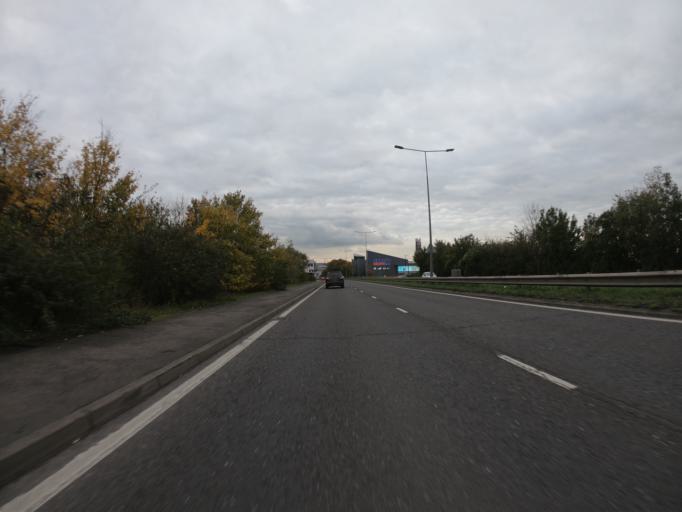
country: GB
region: England
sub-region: Kent
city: West Thurrock
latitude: 51.4877
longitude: 0.2728
